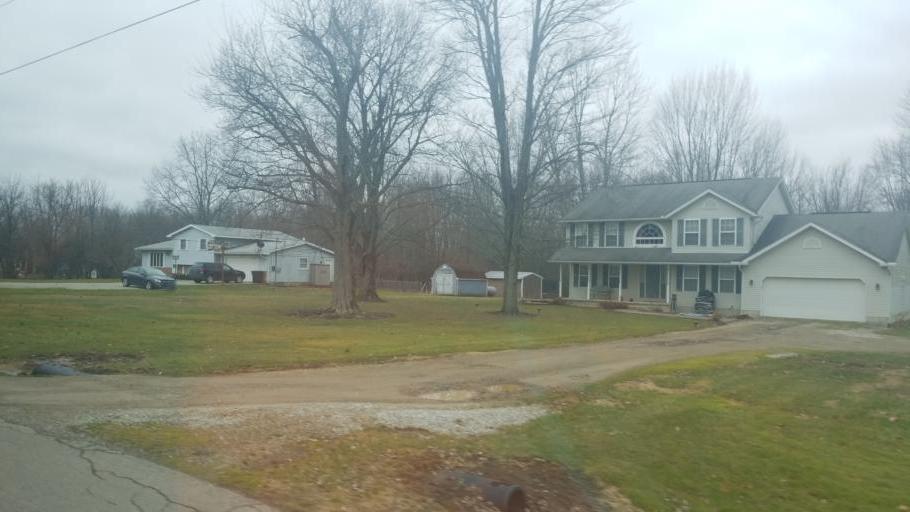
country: US
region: Ohio
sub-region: Crawford County
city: Crestline
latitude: 40.7937
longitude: -82.7323
